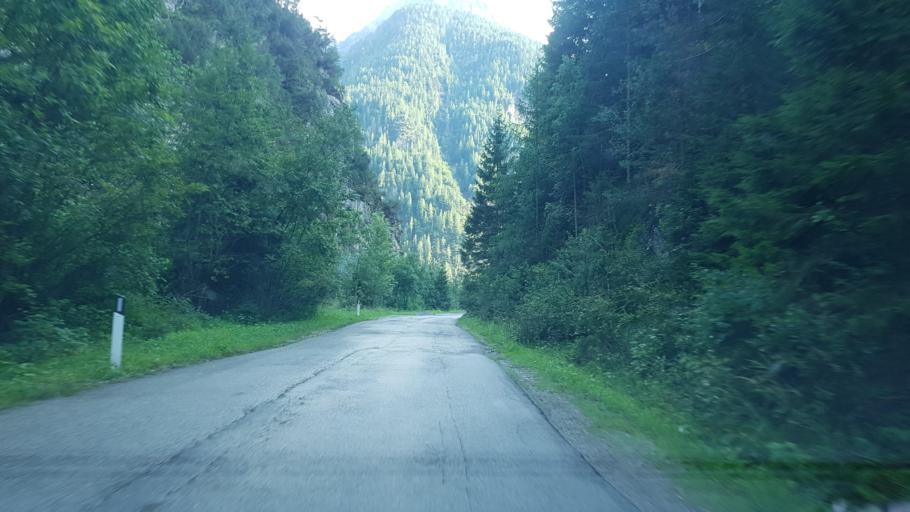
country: IT
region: Veneto
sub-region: Provincia di Belluno
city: San Pietro di Cadore
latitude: 46.5880
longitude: 12.6273
